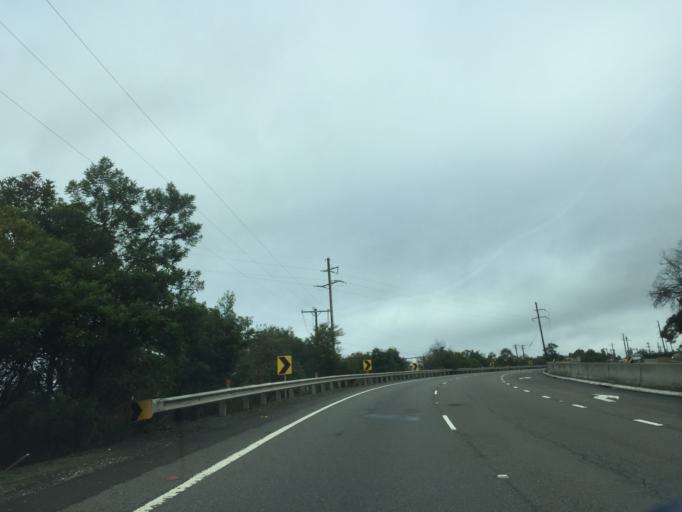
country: AU
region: New South Wales
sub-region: Blue Mountains Municipality
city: Hazelbrook
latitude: -33.7053
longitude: 150.5295
